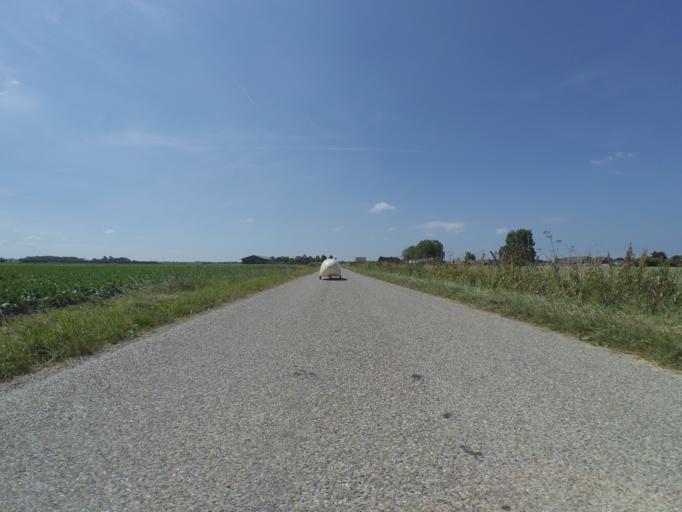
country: NL
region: North Brabant
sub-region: Gemeente Steenbergen
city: Nieuw-Vossemeer
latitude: 51.6233
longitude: 4.1823
